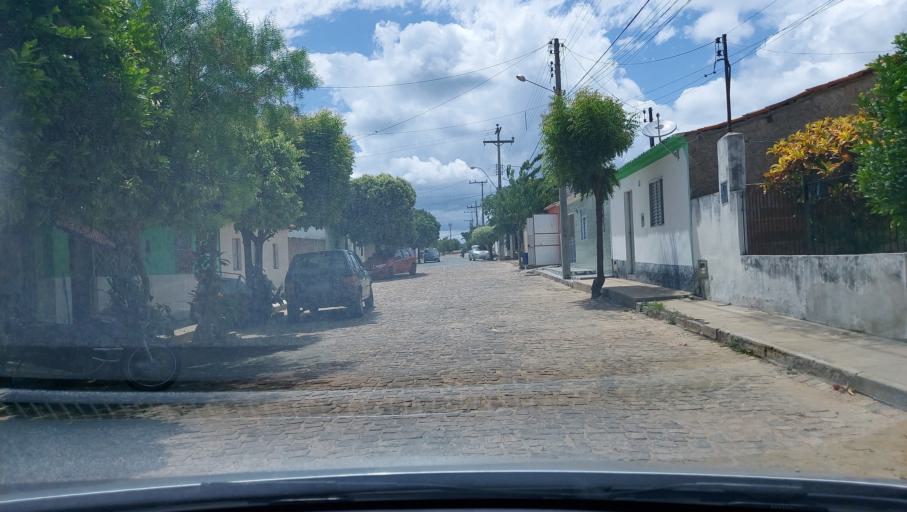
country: BR
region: Bahia
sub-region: Oliveira Dos Brejinhos
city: Beira Rio
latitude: -11.9989
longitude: -42.6295
